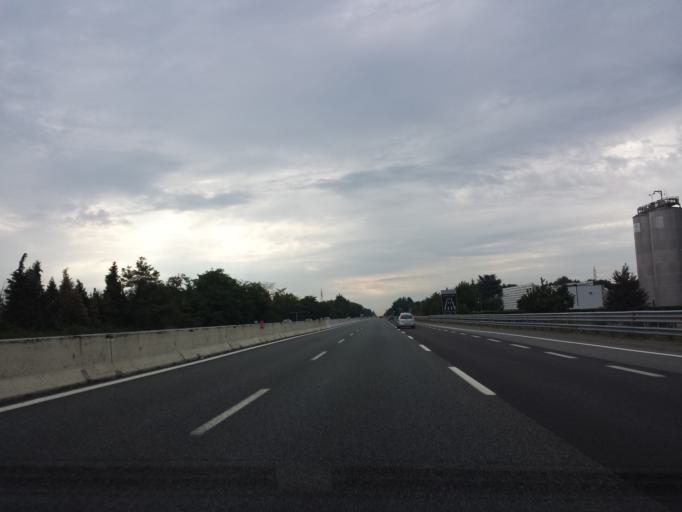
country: IT
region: Lombardy
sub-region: Provincia di Varese
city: Olgiate Olona
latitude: 45.6376
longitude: 8.8629
